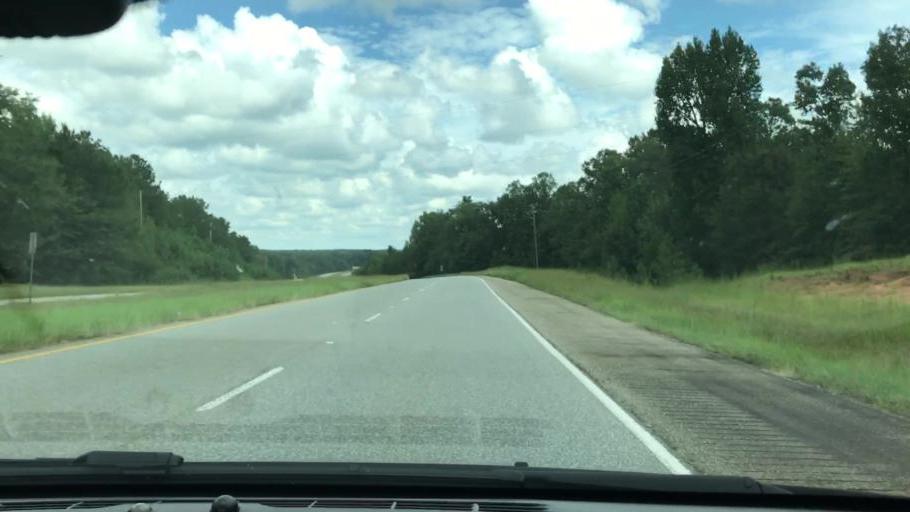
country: US
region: Georgia
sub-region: Stewart County
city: Lumpkin
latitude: 32.1435
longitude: -84.8264
